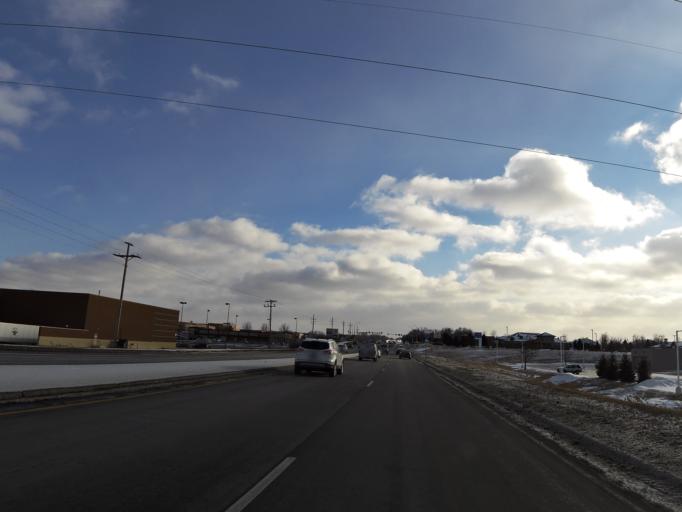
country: US
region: Minnesota
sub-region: Scott County
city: Shakopee
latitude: 44.7768
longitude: -93.5055
